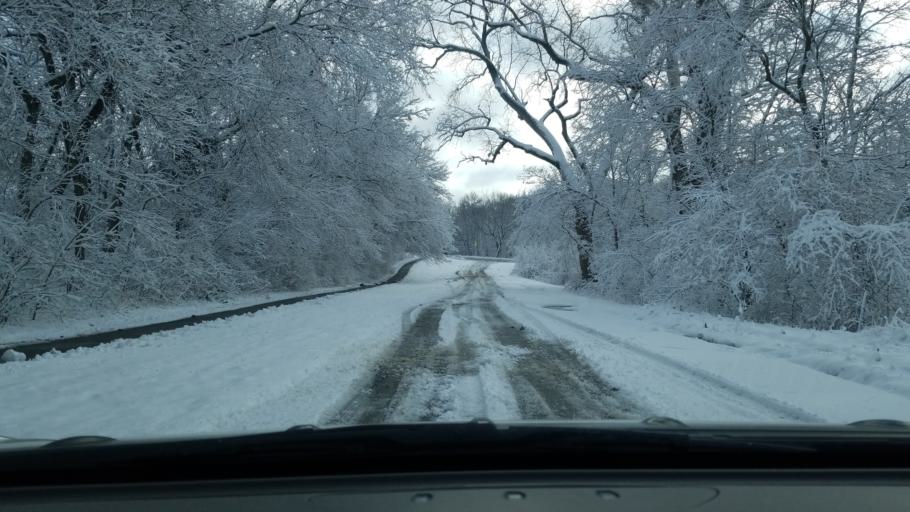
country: US
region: Nebraska
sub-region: Douglas County
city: Omaha
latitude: 41.2210
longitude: -95.9400
